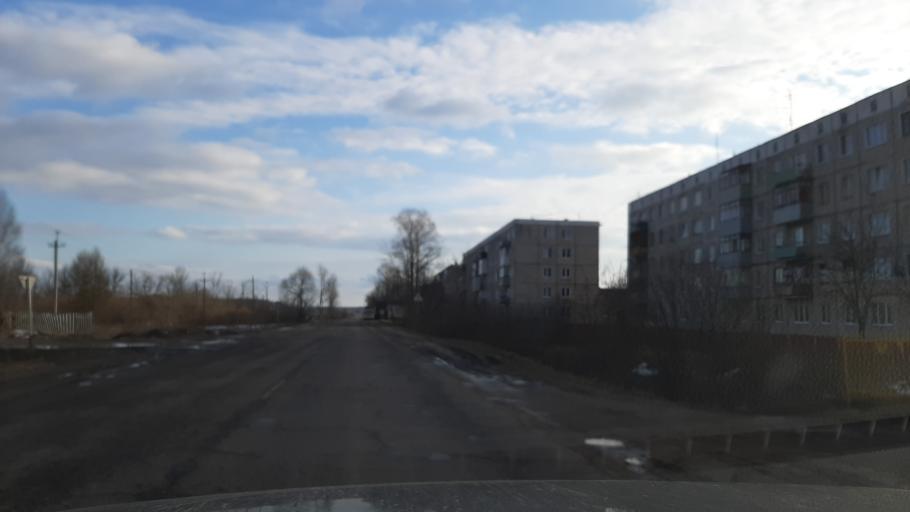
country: RU
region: Ivanovo
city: Novo-Talitsy
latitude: 56.9251
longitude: 40.7374
